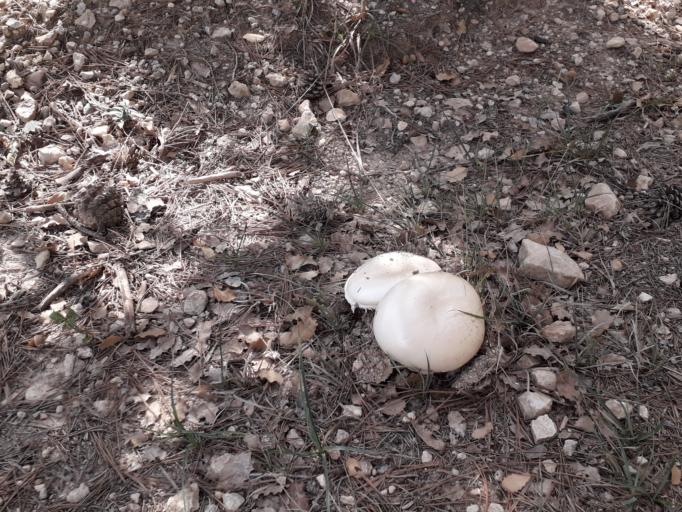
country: ES
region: Catalonia
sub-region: Provincia de Barcelona
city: Bellprat
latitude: 41.5115
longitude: 1.4679
